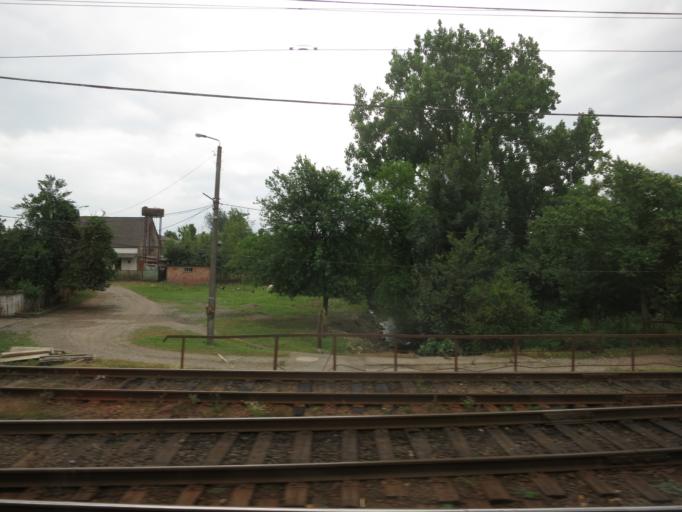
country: GE
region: Imereti
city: Samtredia
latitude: 42.1626
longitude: 42.3506
